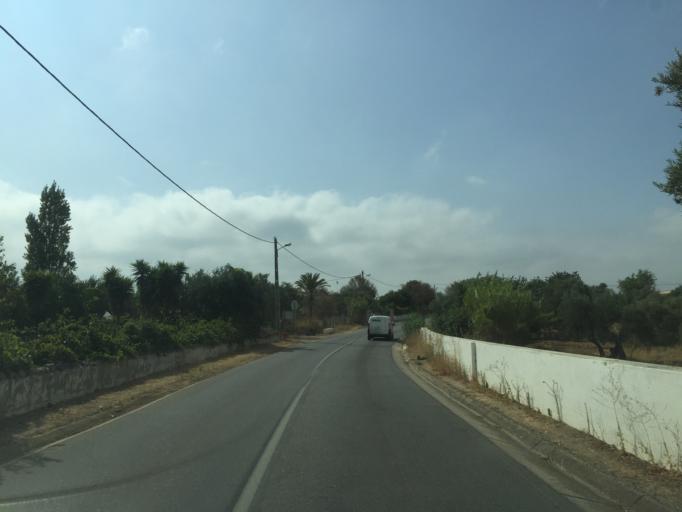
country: PT
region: Faro
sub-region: Sao Bras de Alportel
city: Sao Bras de Alportel
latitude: 37.0905
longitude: -7.8929
